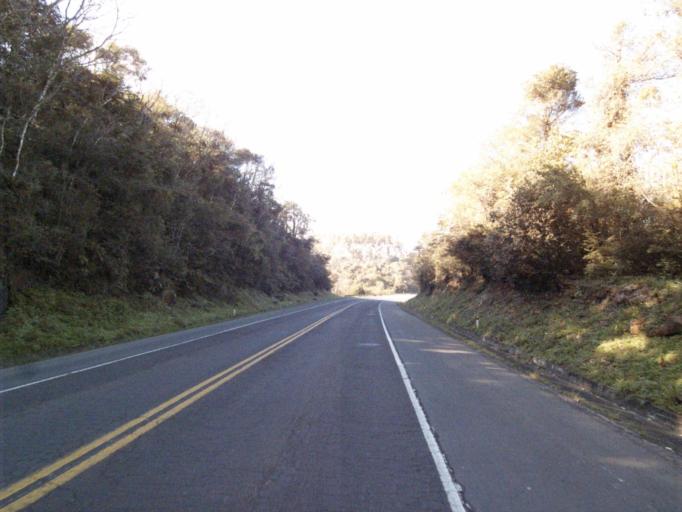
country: BR
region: Rio Grande do Sul
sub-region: Frederico Westphalen
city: Frederico Westphalen
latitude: -26.9987
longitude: -53.2274
